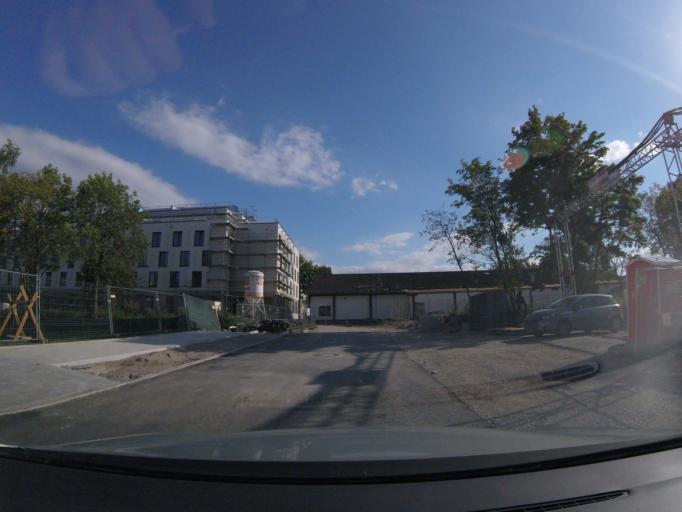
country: DE
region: Bavaria
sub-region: Upper Bavaria
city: Bogenhausen
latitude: 48.1329
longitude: 11.6278
